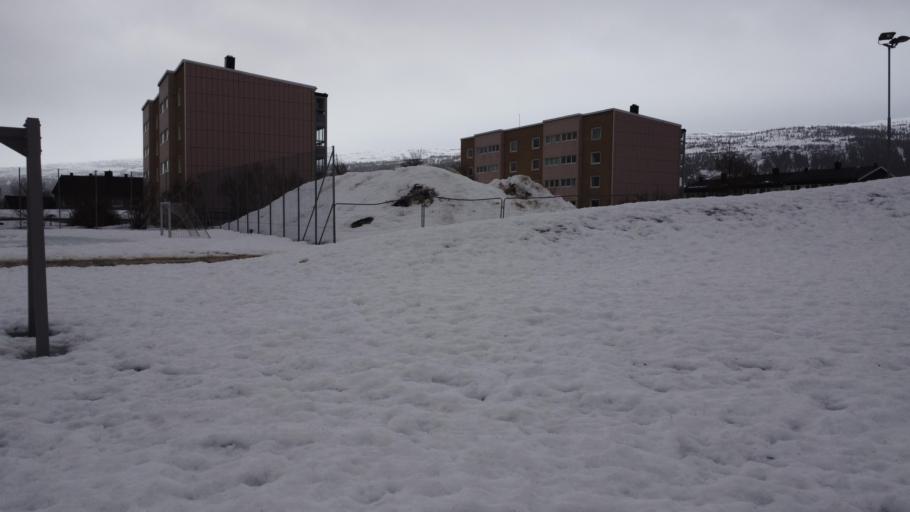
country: NO
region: Nordland
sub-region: Rana
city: Mo i Rana
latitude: 66.3191
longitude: 14.1580
